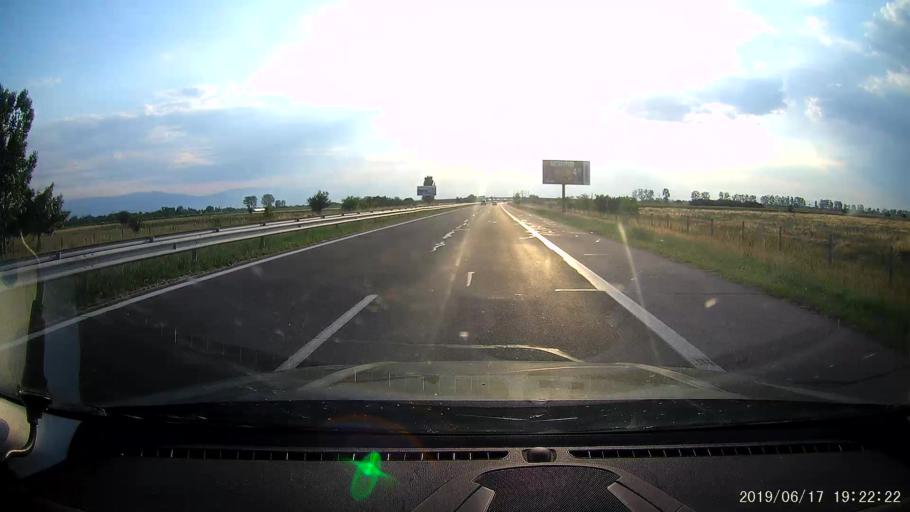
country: BG
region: Pazardzhik
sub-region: Obshtina Pazardzhik
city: Pazardzhik
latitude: 42.2119
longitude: 24.4342
